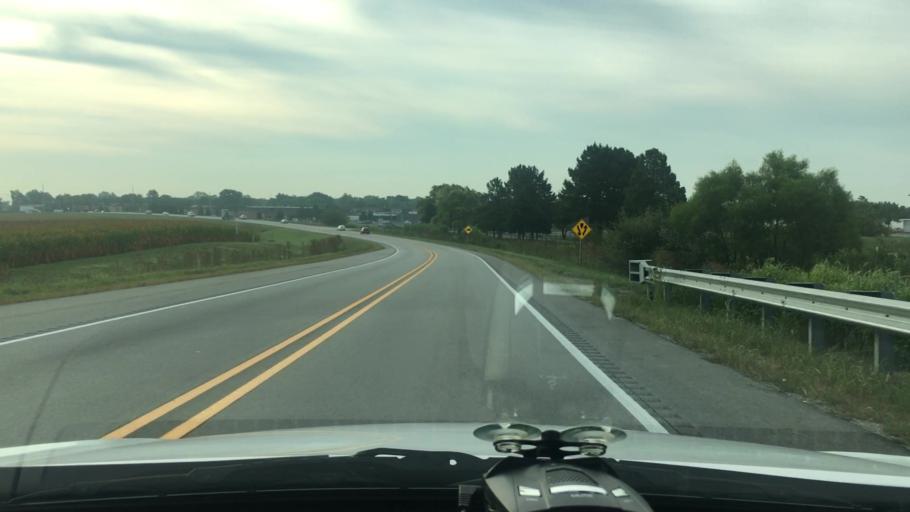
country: US
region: Illinois
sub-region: Champaign County
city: Champaign
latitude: 40.1409
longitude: -88.2844
